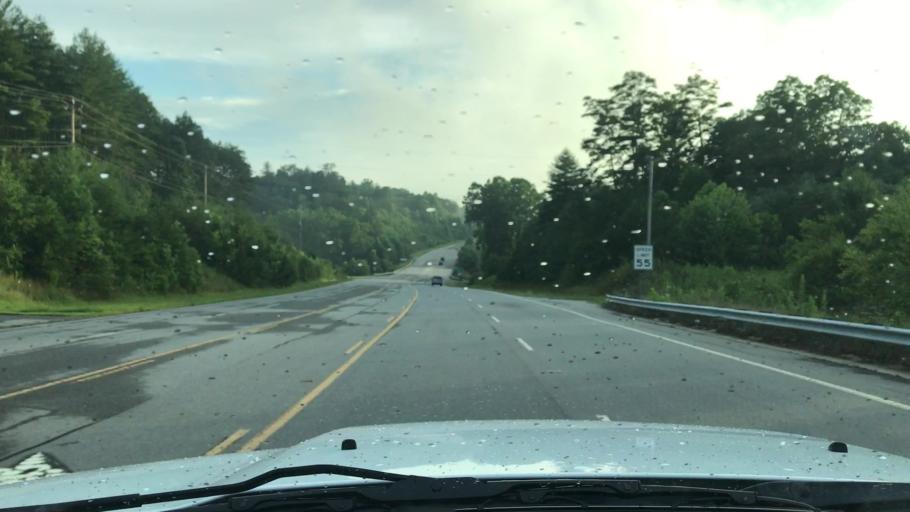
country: US
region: North Carolina
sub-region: Cherokee County
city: Murphy
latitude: 35.0028
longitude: -84.1387
